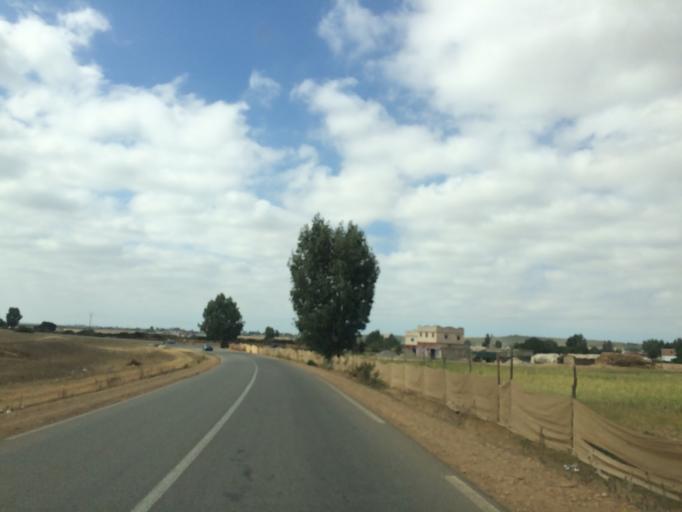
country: MA
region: Gharb-Chrarda-Beni Hssen
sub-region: Kenitra Province
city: Lalla Mimouna
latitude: 34.7702
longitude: -6.0908
